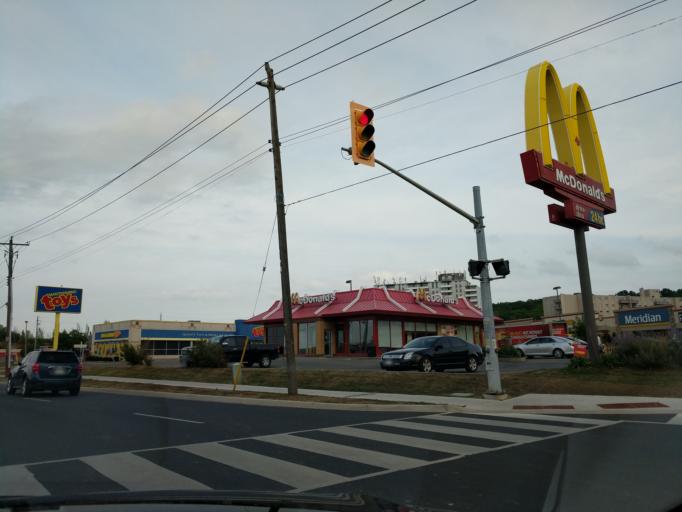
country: CA
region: Ontario
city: Thorold
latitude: 43.1326
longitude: -79.2263
